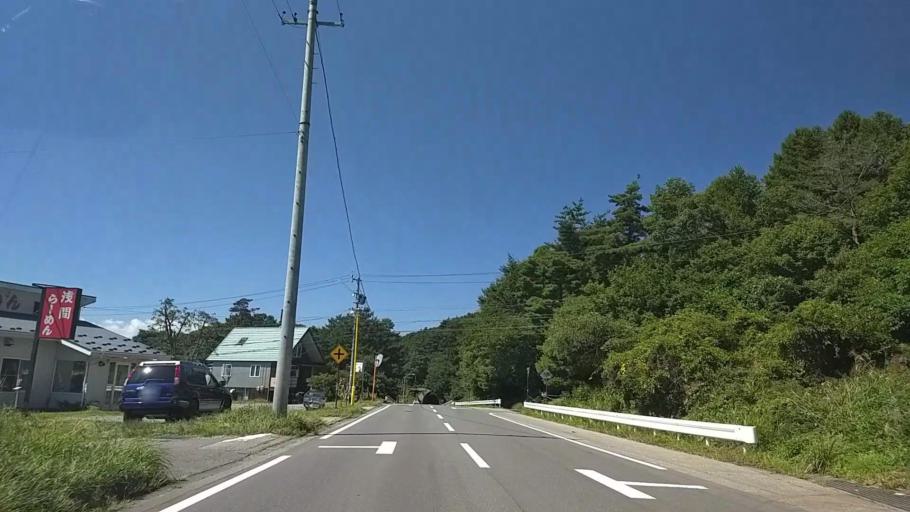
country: JP
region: Nagano
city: Komoro
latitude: 36.3393
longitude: 138.4529
